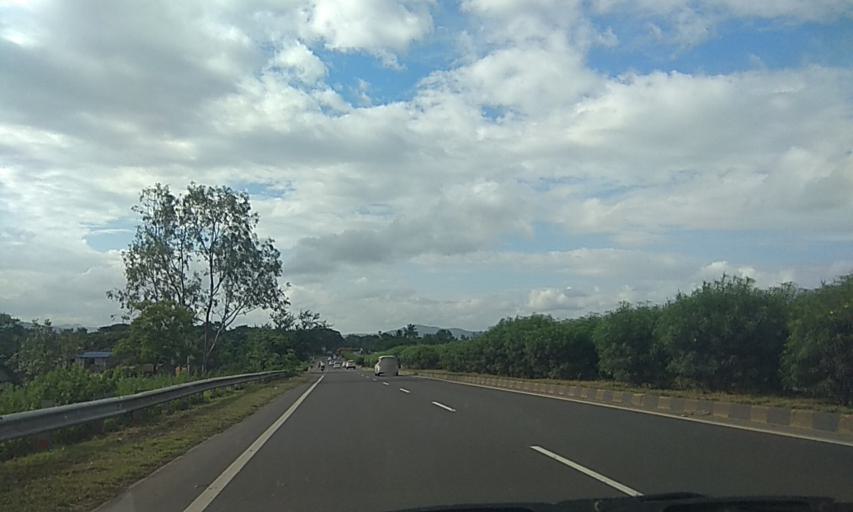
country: IN
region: Maharashtra
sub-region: Satara Division
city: Karad
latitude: 17.1263
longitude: 74.1917
